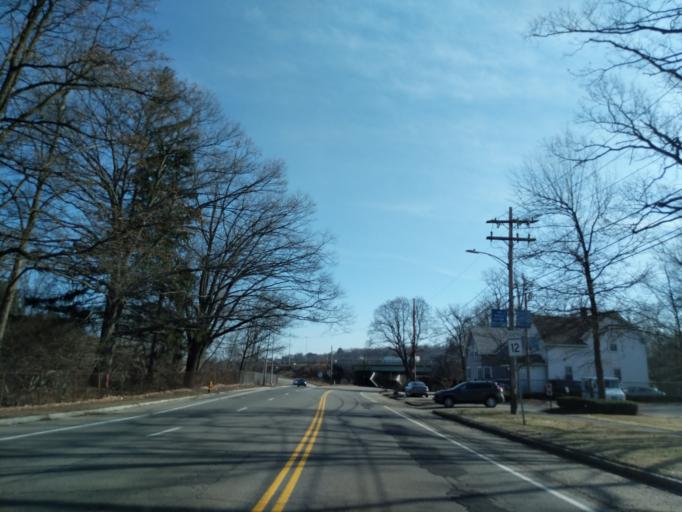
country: US
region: Massachusetts
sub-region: Worcester County
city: Worcester
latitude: 42.2322
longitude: -71.8255
